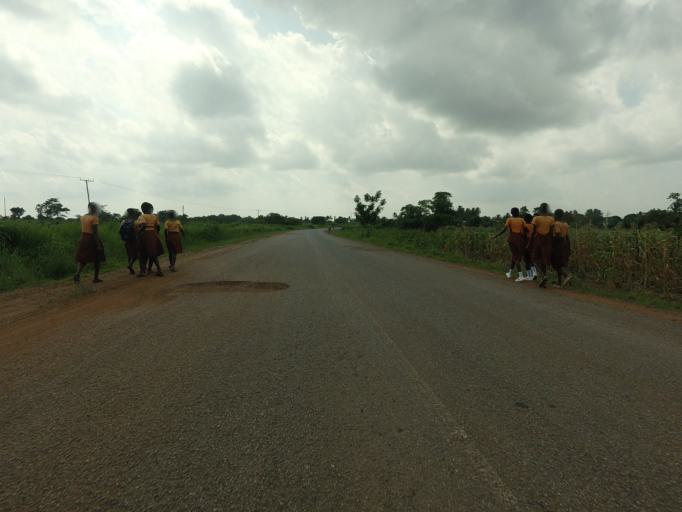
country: GH
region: Volta
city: Ho
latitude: 6.4274
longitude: 0.7333
